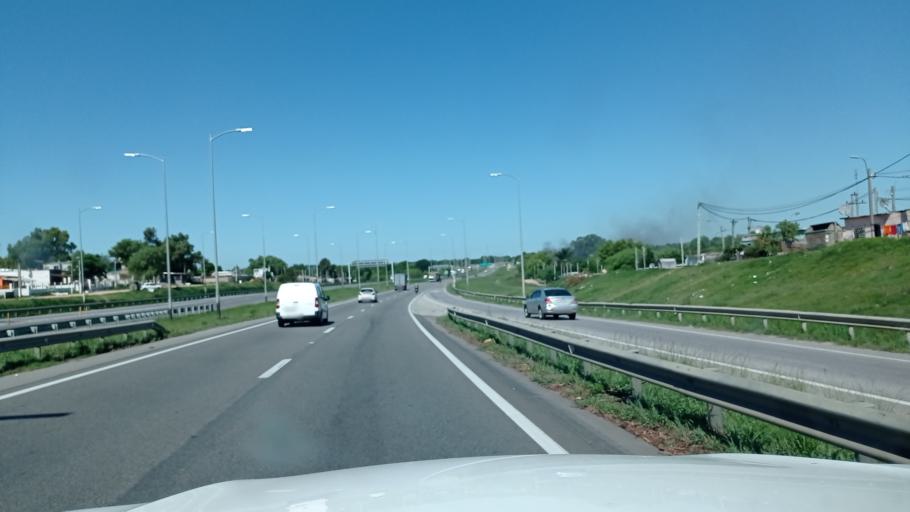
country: UY
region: Montevideo
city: Pajas Blancas
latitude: -34.8527
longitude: -56.2674
